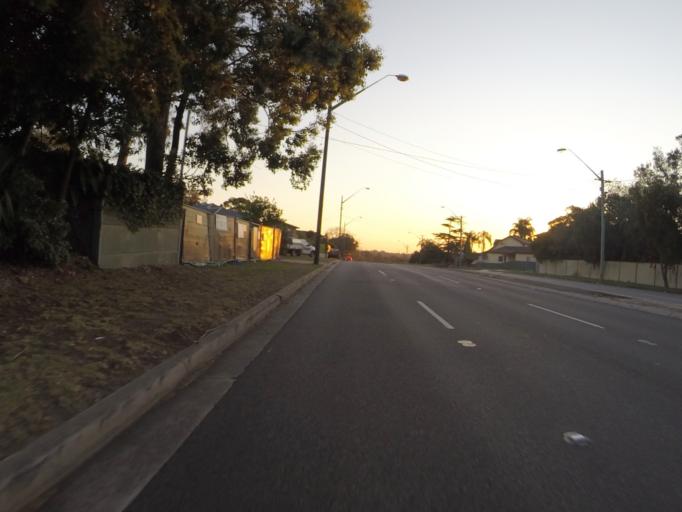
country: AU
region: New South Wales
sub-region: Bankstown
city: Padstow
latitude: -33.9670
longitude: 151.0351
